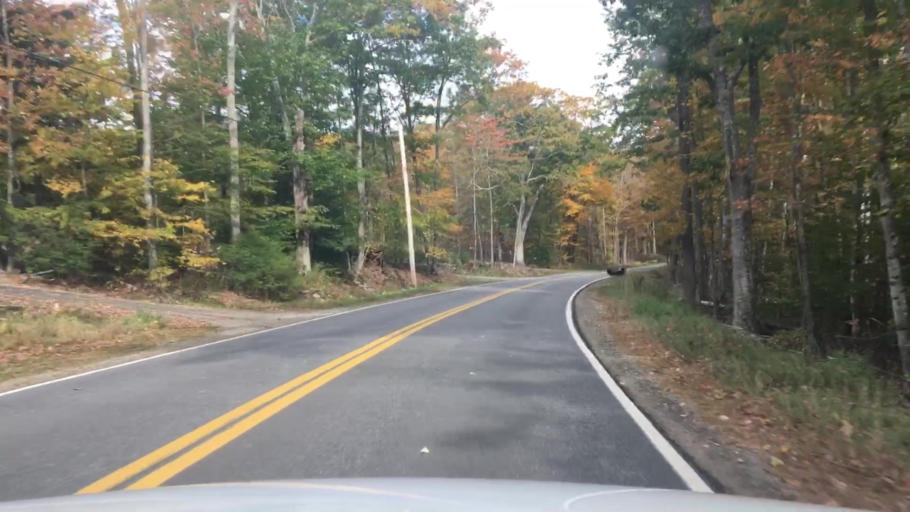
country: US
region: Maine
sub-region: Knox County
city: Hope
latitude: 44.2574
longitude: -69.1322
